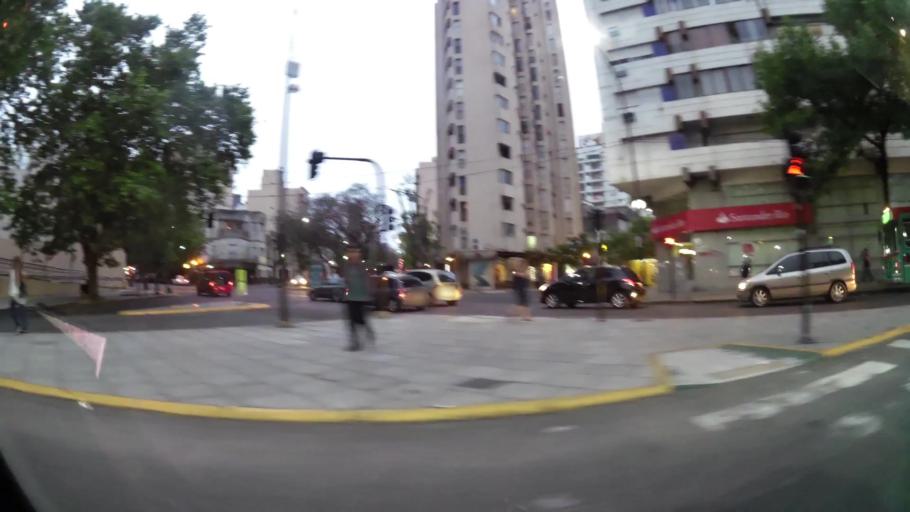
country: AR
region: Buenos Aires
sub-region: Partido de La Plata
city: La Plata
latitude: -34.9215
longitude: -57.9525
